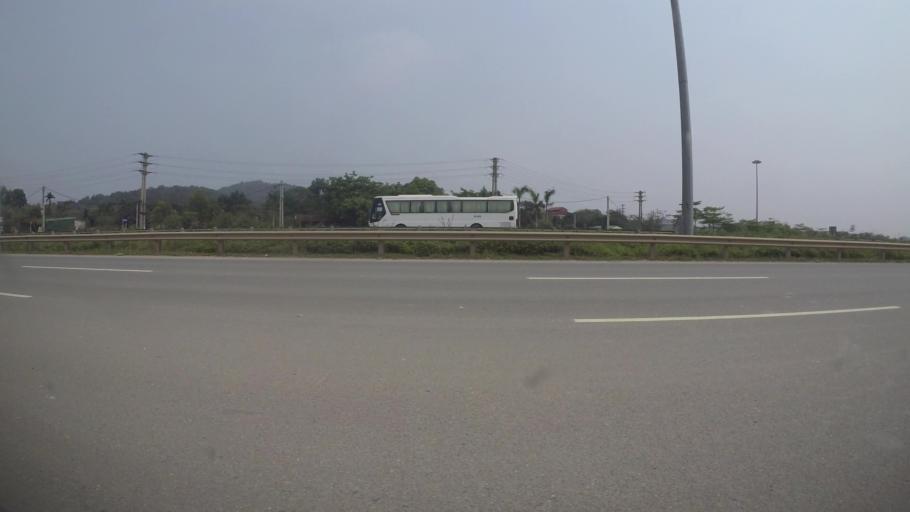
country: VN
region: Ha Noi
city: Lien Quan
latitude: 20.9900
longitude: 105.5210
